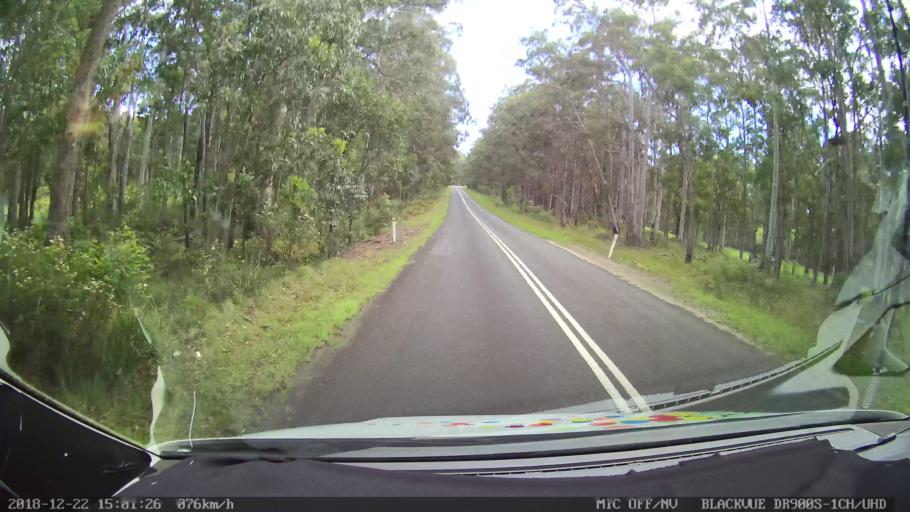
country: AU
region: New South Wales
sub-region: Bellingen
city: Dorrigo
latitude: -30.2543
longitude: 152.4587
